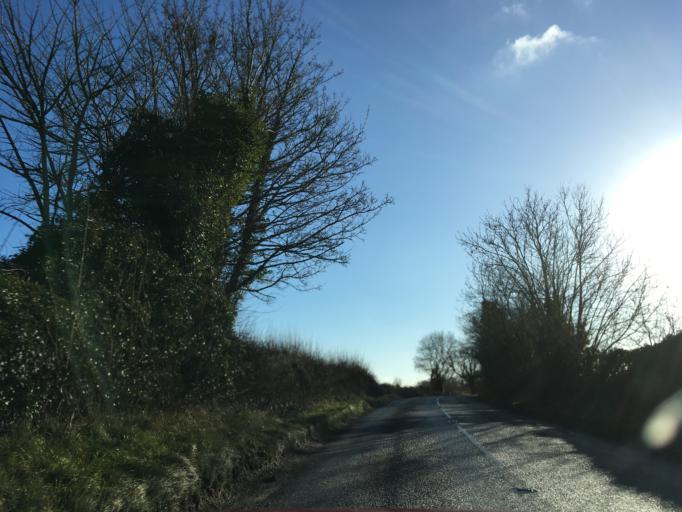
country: GB
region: England
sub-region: Wiltshire
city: Nettleton
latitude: 51.5094
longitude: -2.2334
